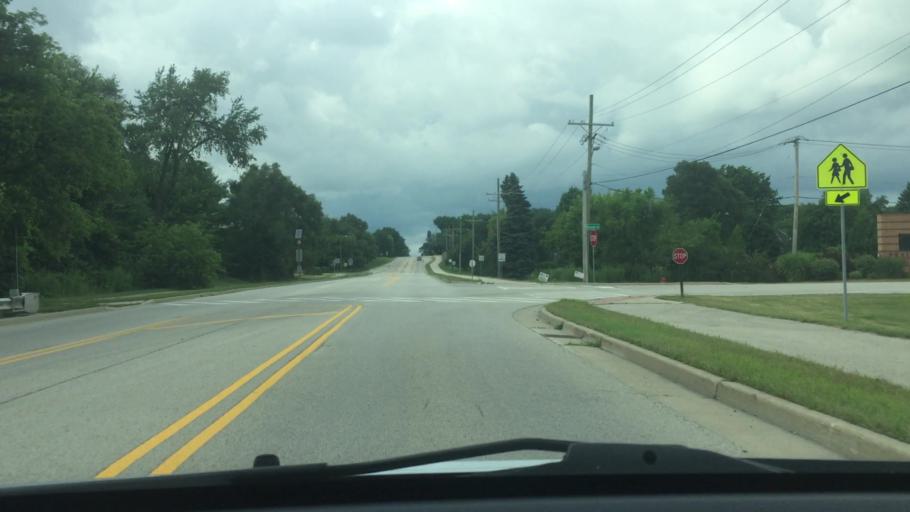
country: US
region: Illinois
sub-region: McHenry County
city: Crystal Lake
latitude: 42.2695
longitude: -88.3208
